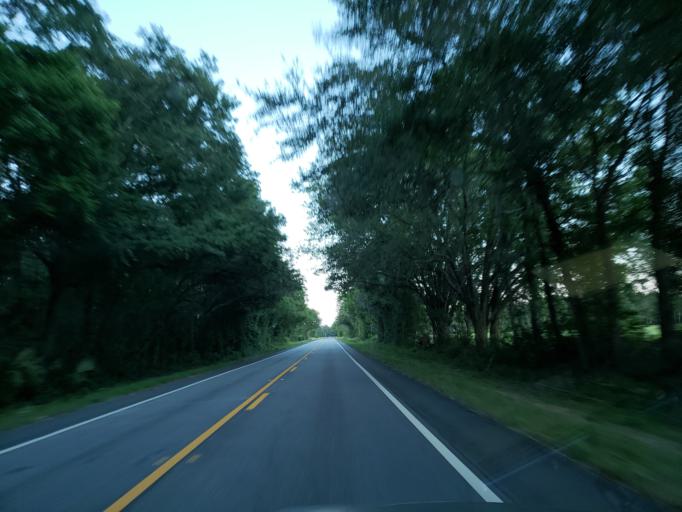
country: US
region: Florida
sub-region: Hamilton County
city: Jasper
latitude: 30.5548
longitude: -83.0759
